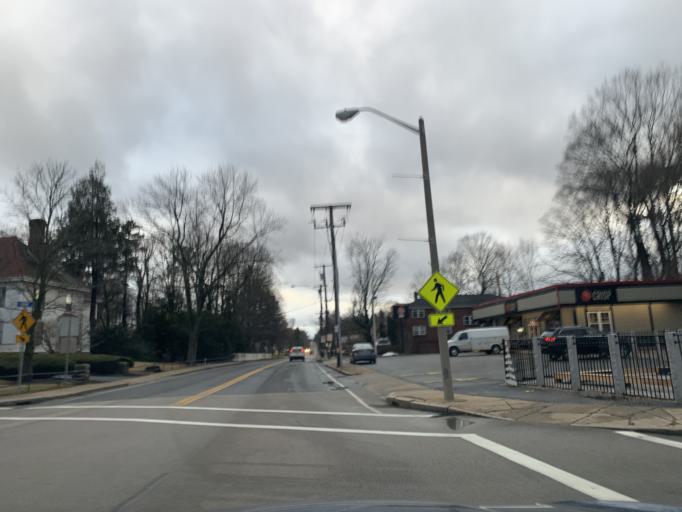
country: US
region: Massachusetts
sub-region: Norfolk County
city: Walpole
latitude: 42.1444
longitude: -71.2541
